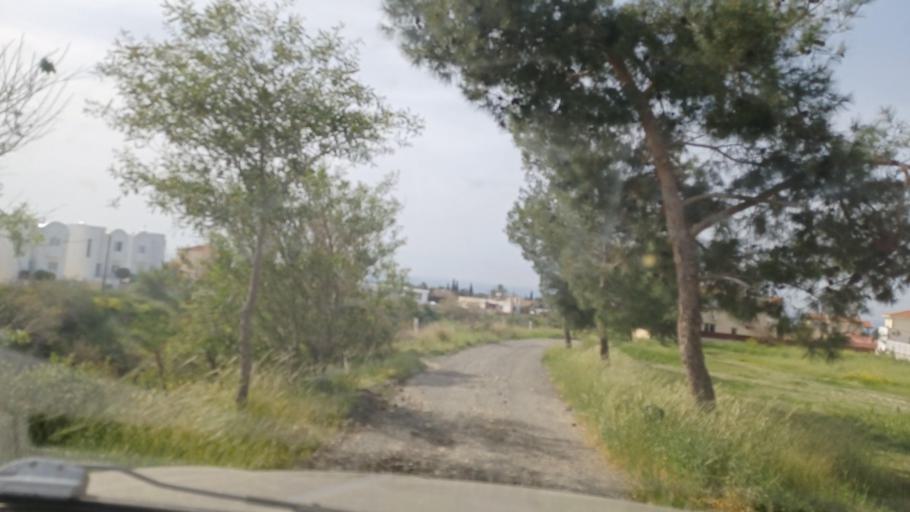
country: CY
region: Pafos
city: Paphos
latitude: 34.7605
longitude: 32.4728
